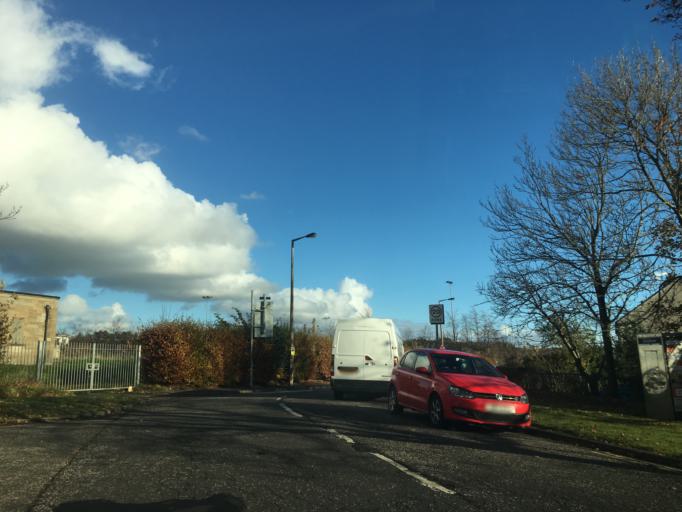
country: GB
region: Scotland
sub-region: Edinburgh
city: Colinton
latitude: 55.9137
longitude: -3.2390
